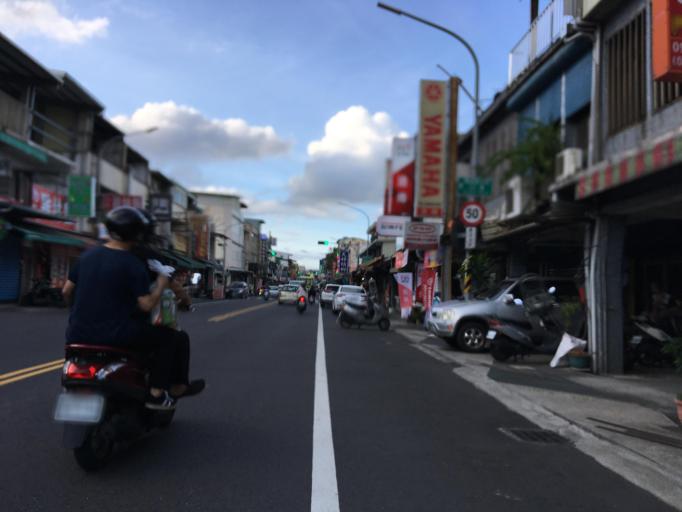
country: TW
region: Taiwan
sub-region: Yilan
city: Yilan
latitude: 24.6653
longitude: 121.7675
